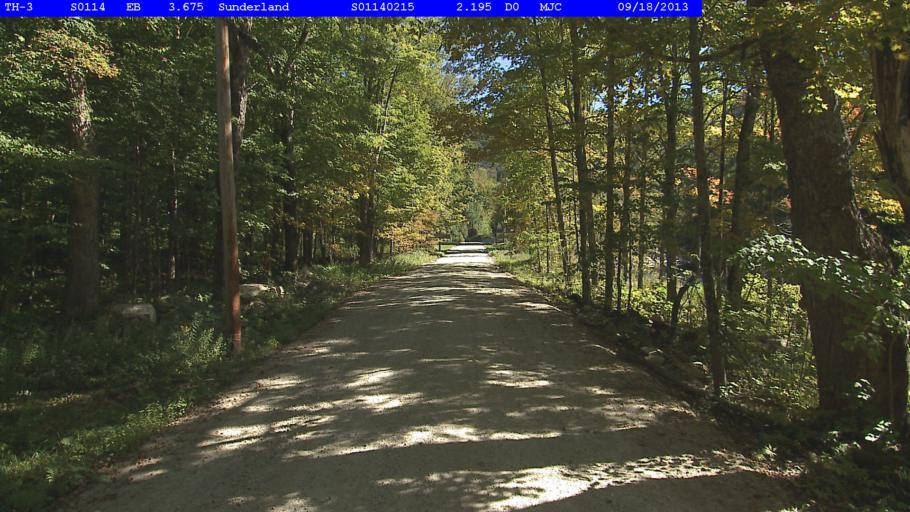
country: US
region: Vermont
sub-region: Bennington County
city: Arlington
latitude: 43.0430
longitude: -73.1124
